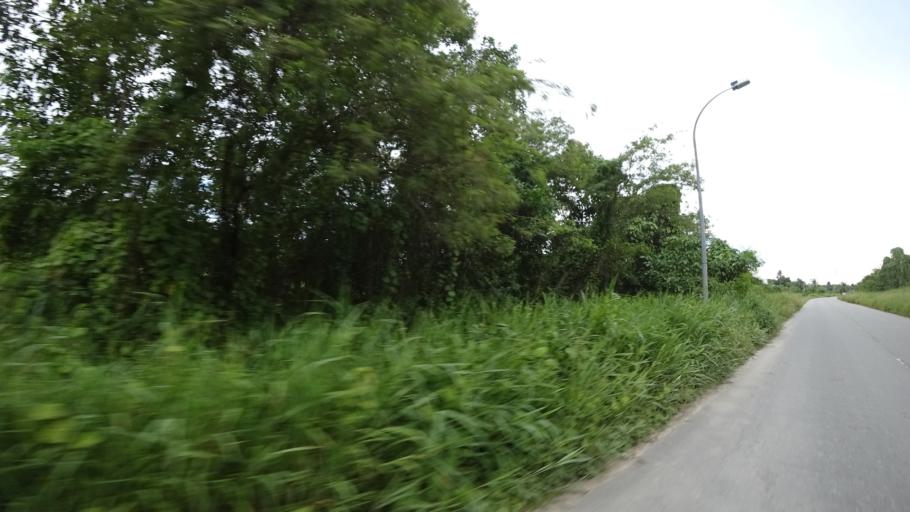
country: BN
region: Brunei and Muara
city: Bandar Seri Begawan
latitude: 4.8747
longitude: 114.8643
